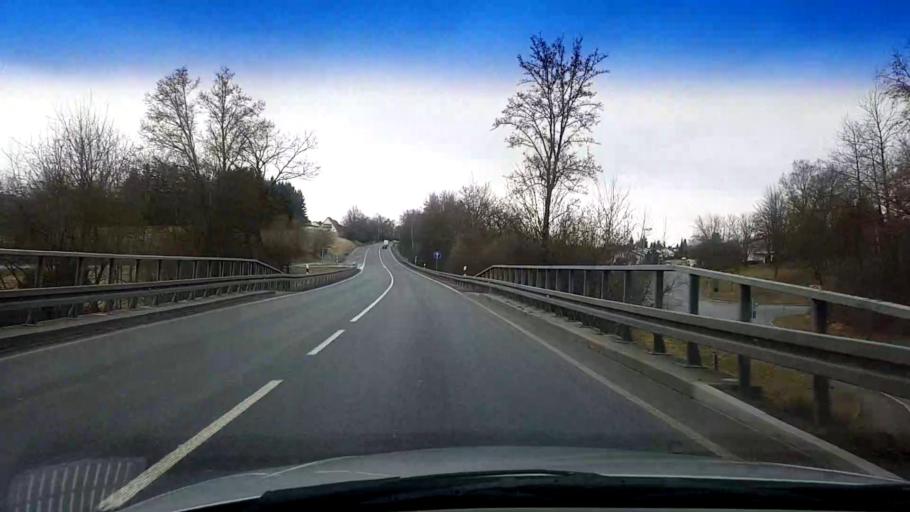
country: DE
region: Bavaria
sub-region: Upper Franconia
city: Kulmbach
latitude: 50.0783
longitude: 11.4673
